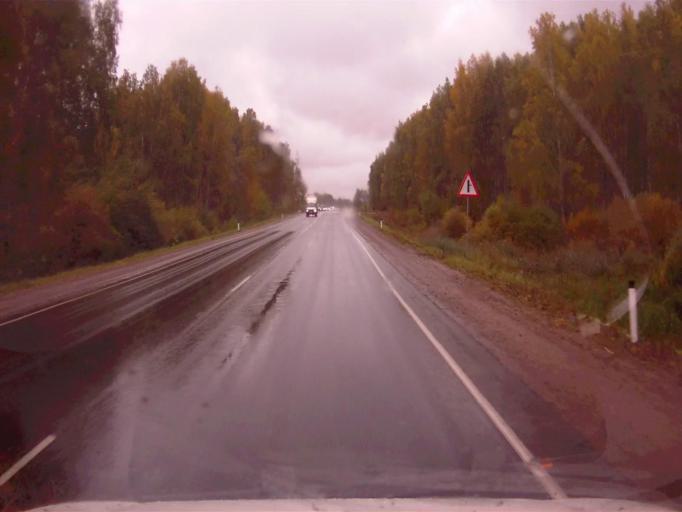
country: RU
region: Chelyabinsk
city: Argayash
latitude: 55.4663
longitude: 60.9103
